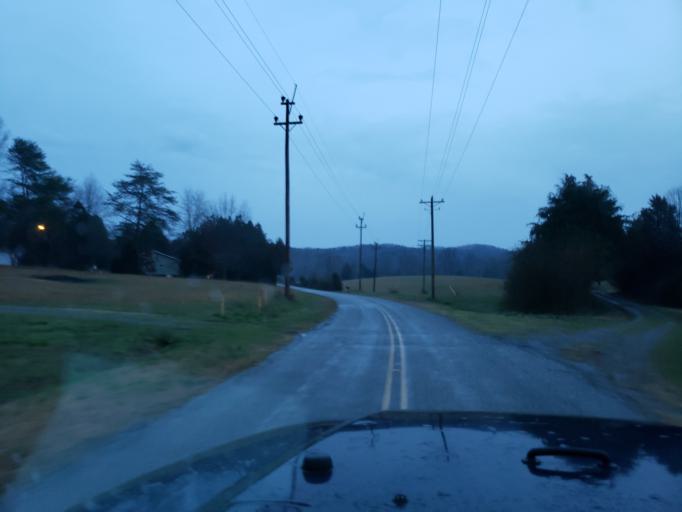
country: US
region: North Carolina
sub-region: Cleveland County
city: White Plains
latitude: 35.1498
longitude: -81.4146
